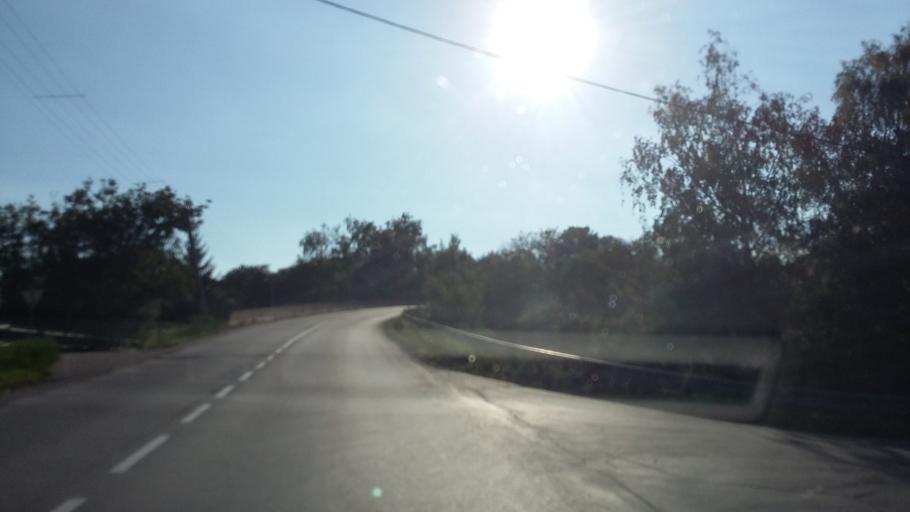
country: CZ
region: South Moravian
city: Ricany
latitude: 49.2157
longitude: 16.3866
